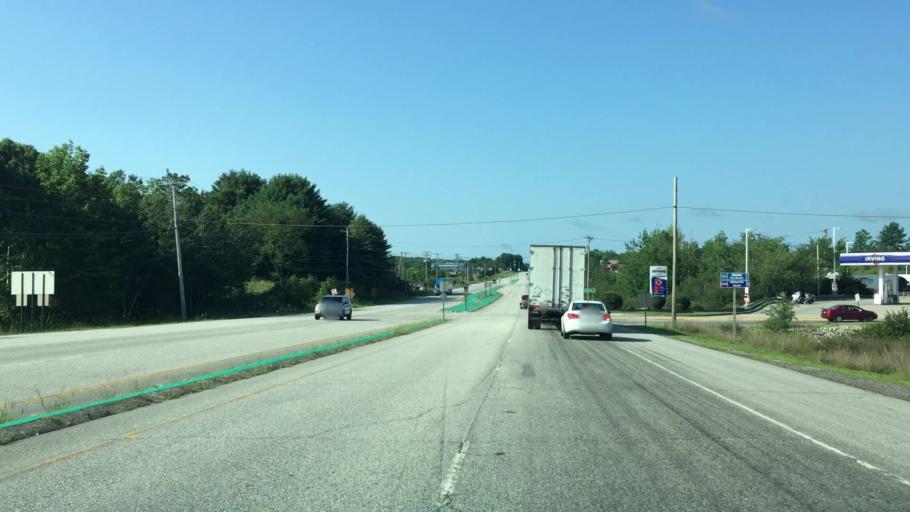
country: US
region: Maine
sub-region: Androscoggin County
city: Auburn
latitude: 44.0352
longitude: -70.2663
